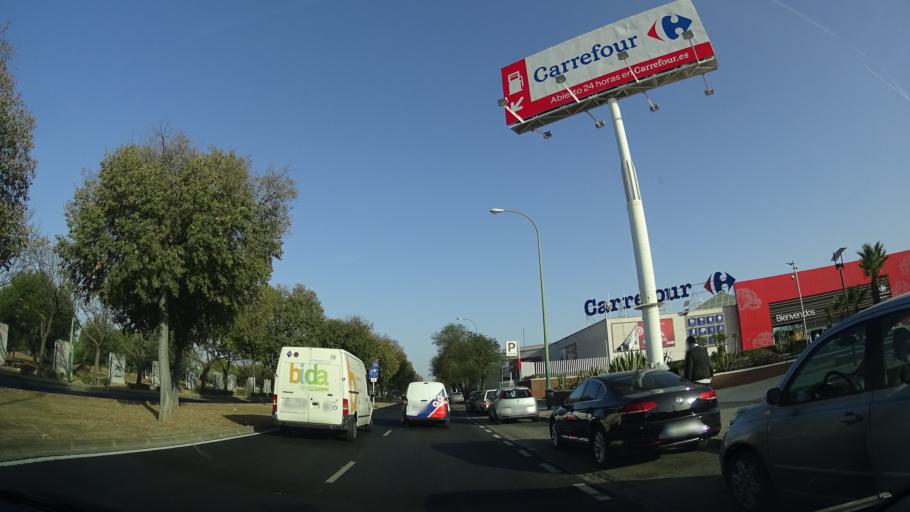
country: ES
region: Andalusia
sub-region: Provincia de Sevilla
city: Sevilla
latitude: 37.4167
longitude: -5.9746
